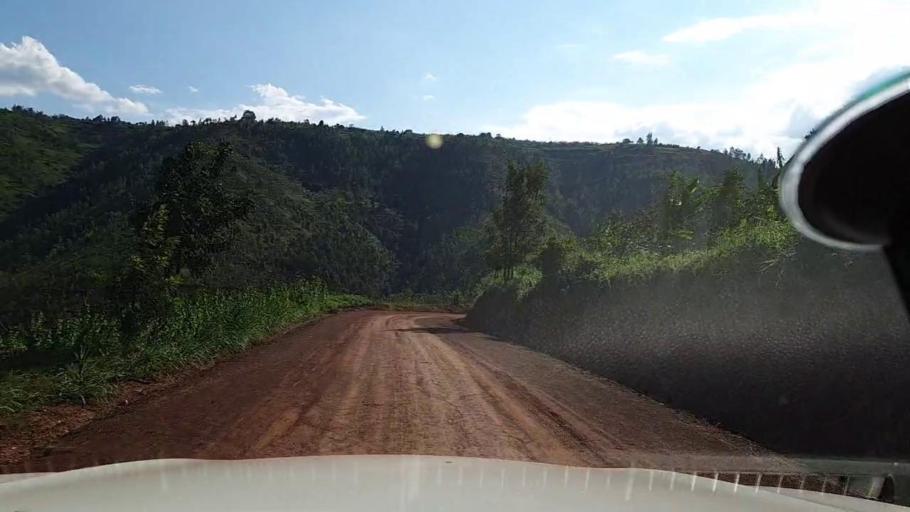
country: RW
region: Kigali
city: Kigali
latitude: -1.8450
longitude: 29.8572
